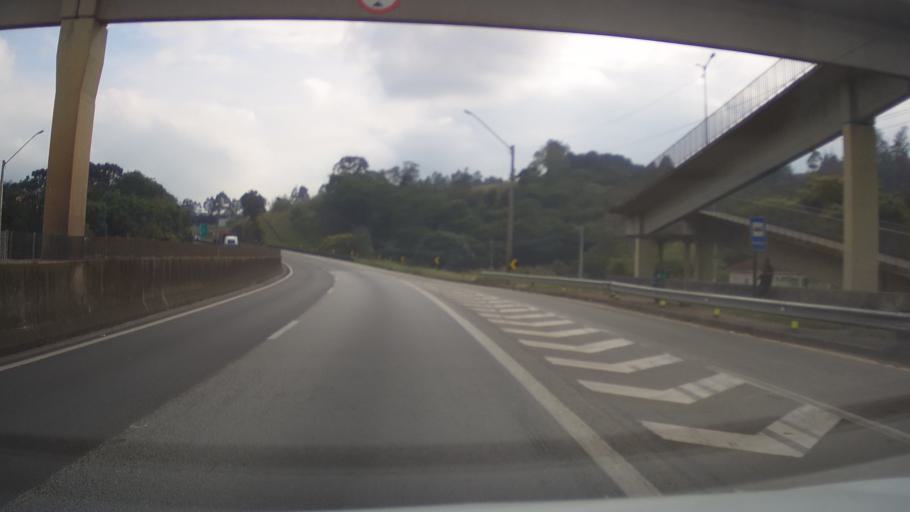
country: BR
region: Minas Gerais
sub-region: Extrema
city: Extrema
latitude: -22.8938
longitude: -46.4153
